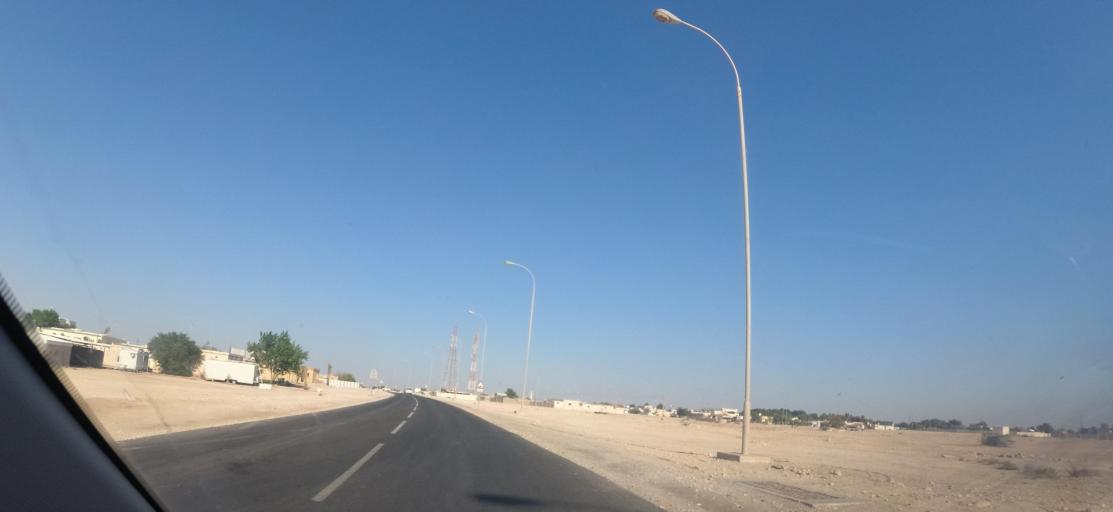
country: QA
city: Al Ghuwayriyah
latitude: 25.8259
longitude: 51.2454
